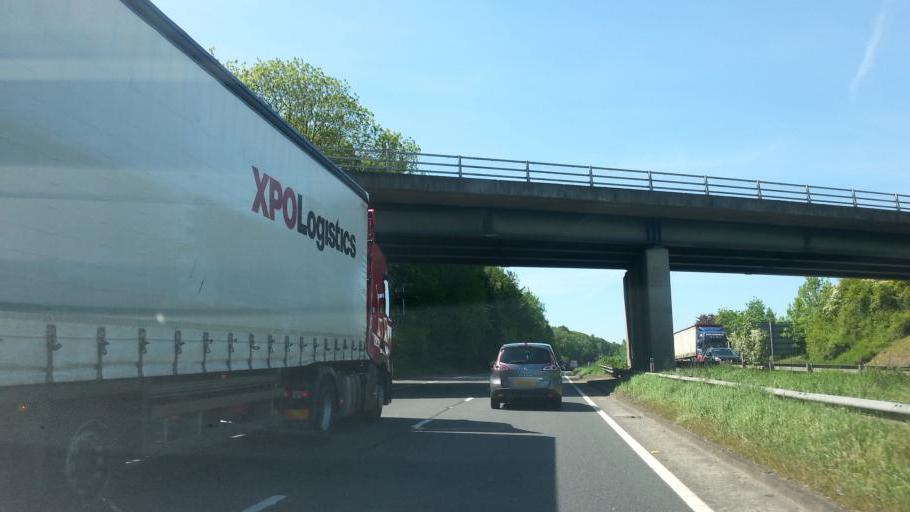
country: GB
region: England
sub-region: Hampshire
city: Andover
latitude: 51.1872
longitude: -1.4090
